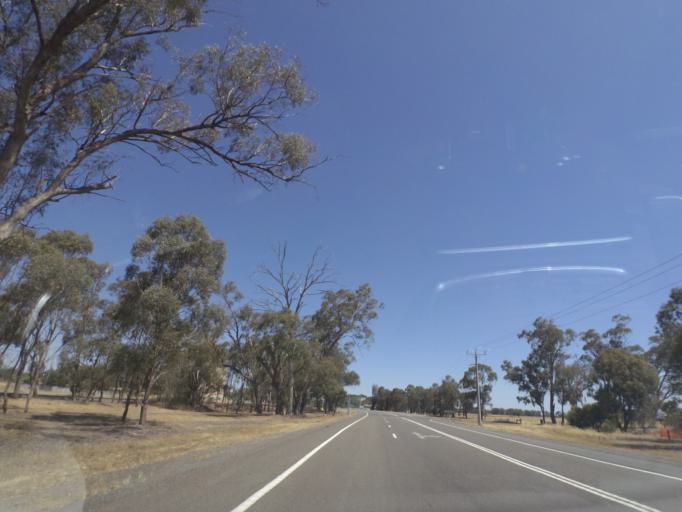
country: AU
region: Victoria
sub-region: Greater Shepparton
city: Shepparton
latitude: -36.2356
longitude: 145.4316
